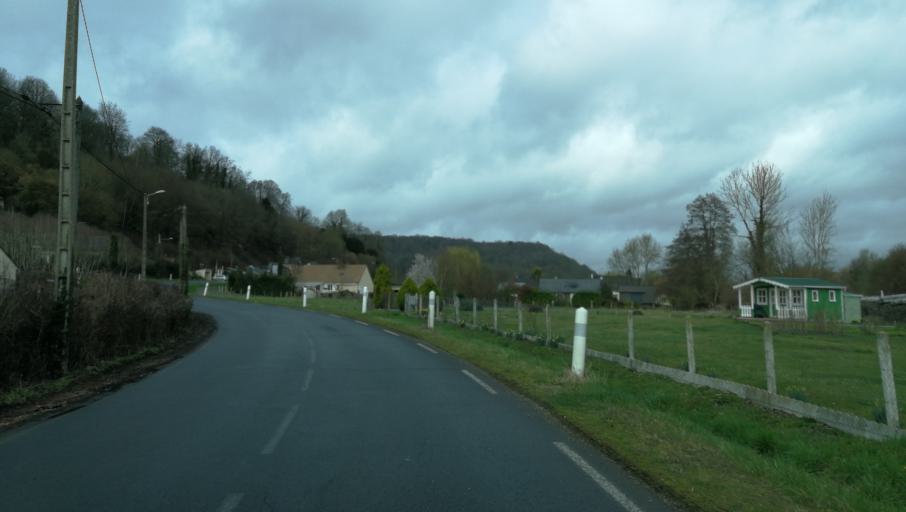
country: FR
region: Haute-Normandie
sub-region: Departement de l'Eure
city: Brionne
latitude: 49.2295
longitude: 0.6942
